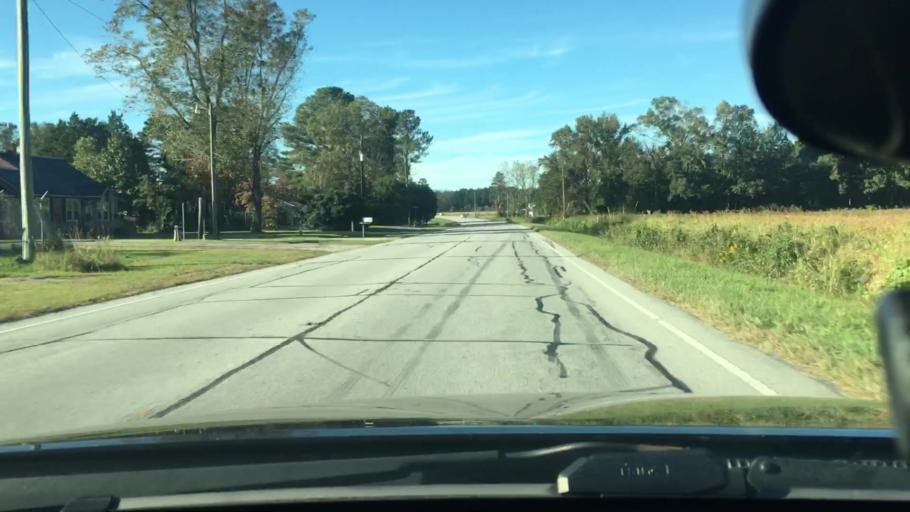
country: US
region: North Carolina
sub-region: Craven County
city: Vanceboro
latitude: 35.3170
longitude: -77.1631
